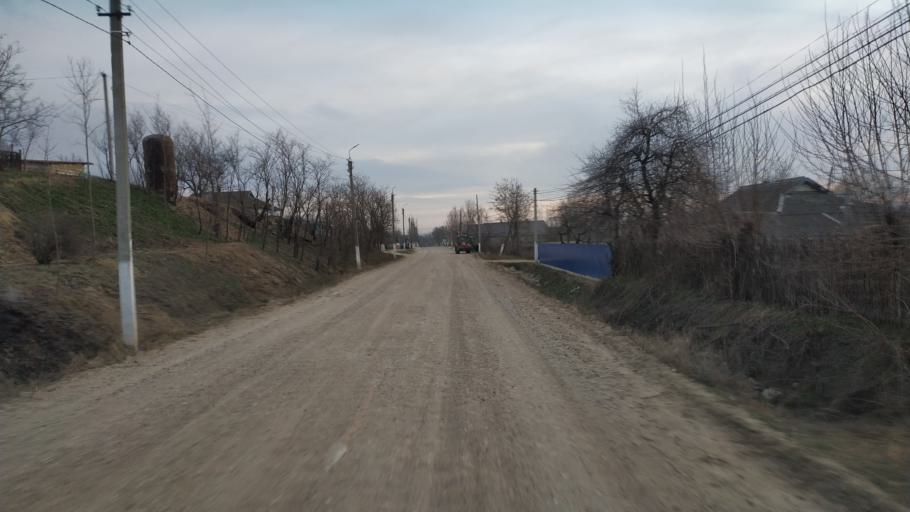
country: MD
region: Hincesti
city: Dancu
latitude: 46.7580
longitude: 28.2087
